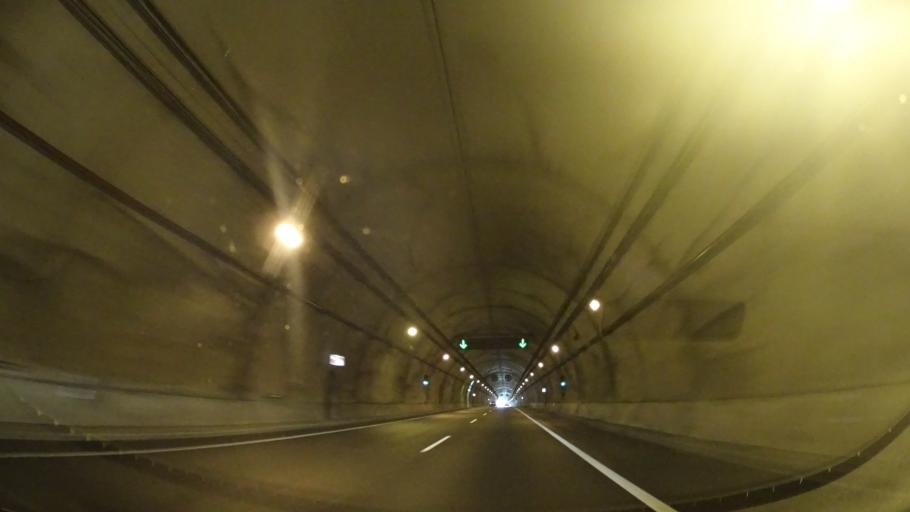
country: ES
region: Asturias
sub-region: Province of Asturias
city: Arriba
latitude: 43.4888
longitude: -5.5304
